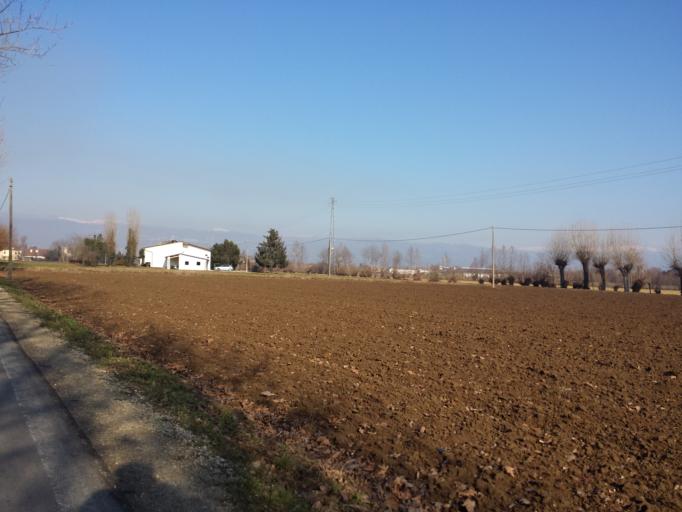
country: IT
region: Veneto
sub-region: Provincia di Vicenza
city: Sandrigo
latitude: 45.6404
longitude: 11.6033
